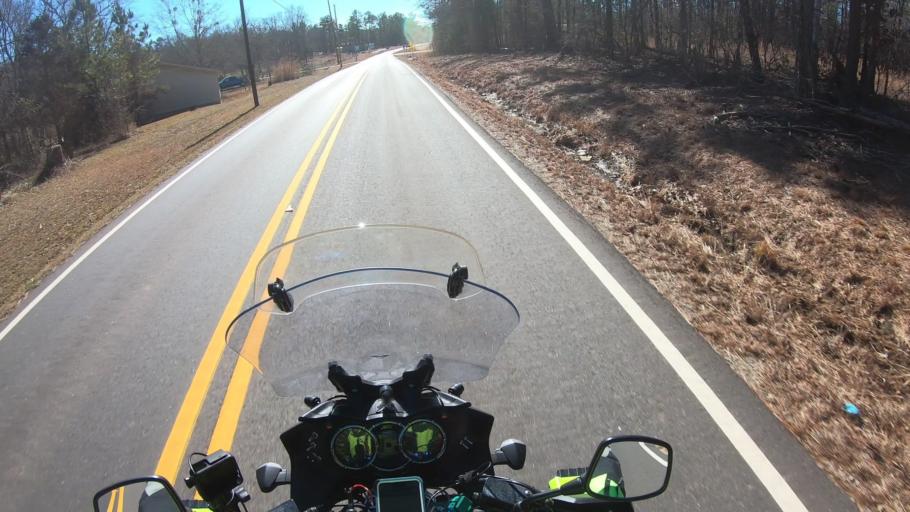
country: US
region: Alabama
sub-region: Clay County
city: Lineville
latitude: 33.4174
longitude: -85.7814
